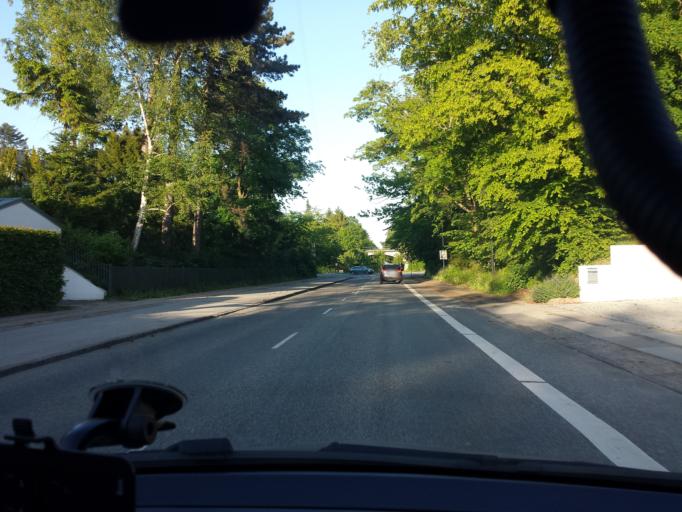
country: DK
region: Capital Region
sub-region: Gentofte Kommune
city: Charlottenlund
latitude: 55.7684
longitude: 12.5831
